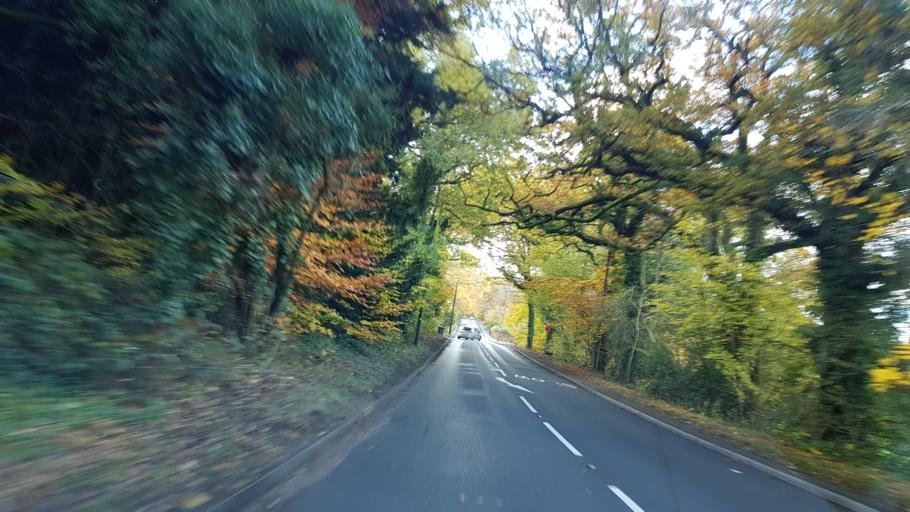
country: GB
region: England
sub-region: Surrey
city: Haslemere
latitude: 51.1008
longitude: -0.6958
